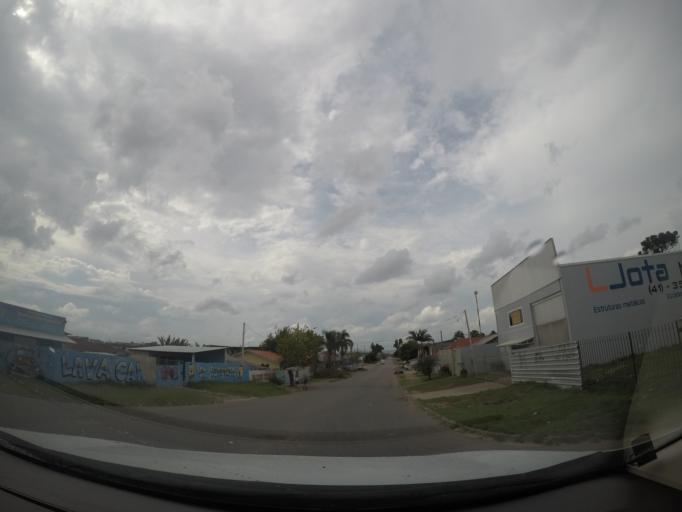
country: BR
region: Parana
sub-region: Sao Jose Dos Pinhais
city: Sao Jose dos Pinhais
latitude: -25.5040
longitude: -49.2178
